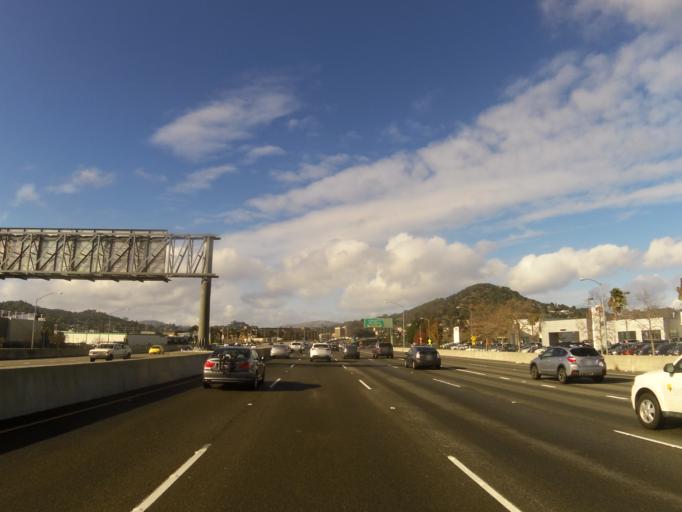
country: US
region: California
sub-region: Marin County
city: San Rafael
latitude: 37.9673
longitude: -122.5180
